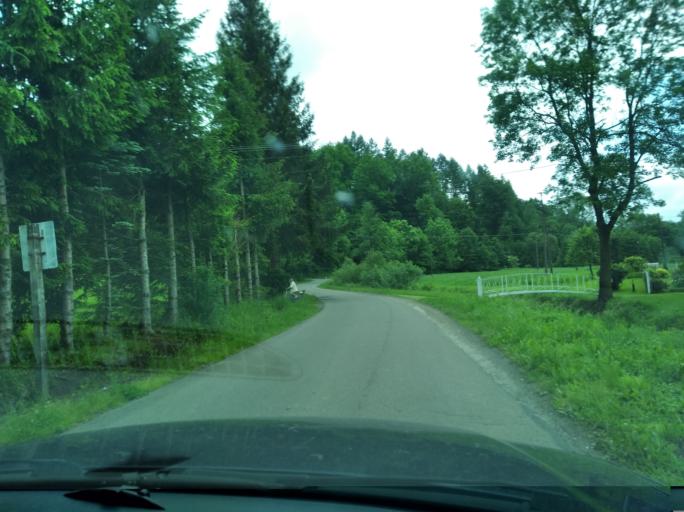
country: PL
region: Subcarpathian Voivodeship
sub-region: Powiat przemyski
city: Dubiecko
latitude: 49.8374
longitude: 22.3975
